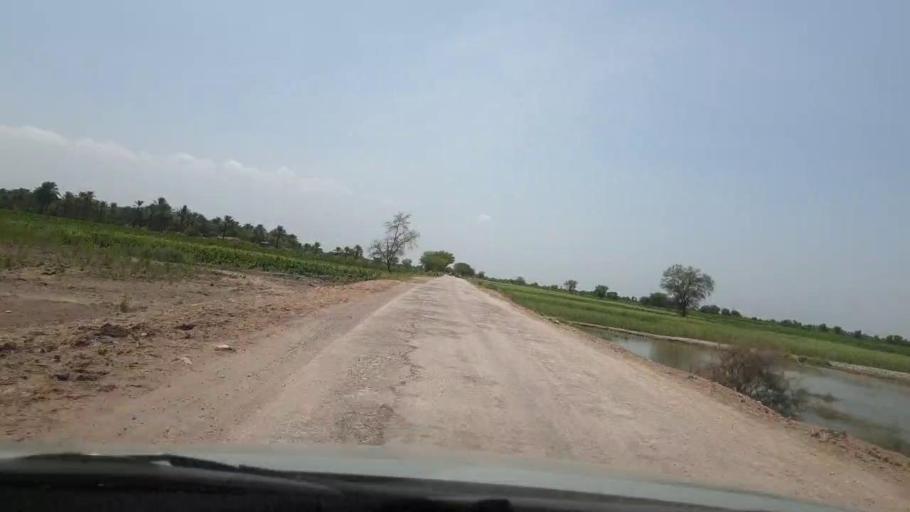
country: PK
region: Sindh
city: Pano Aqil
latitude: 27.6634
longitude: 69.1285
